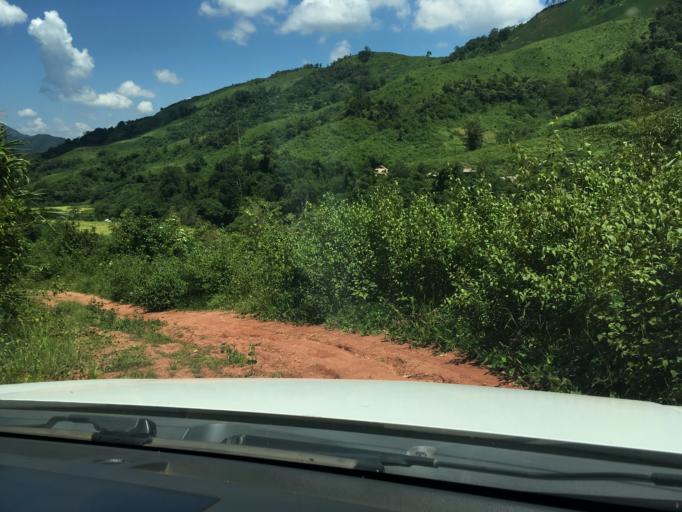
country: LA
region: Phongsali
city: Phongsali
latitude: 21.7889
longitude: 101.8660
